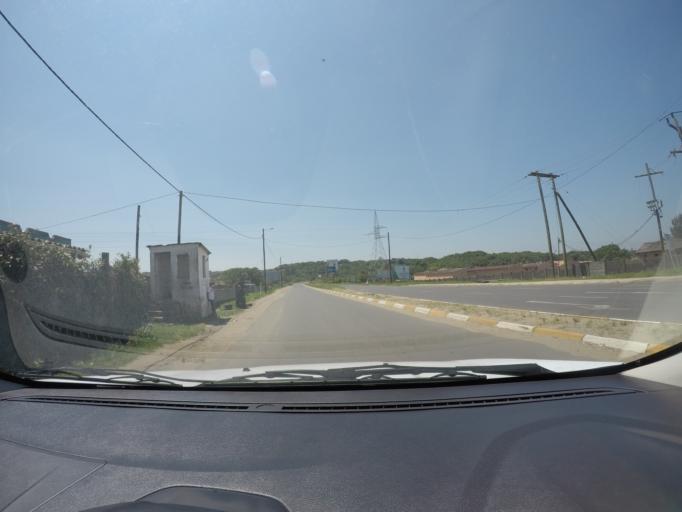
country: ZA
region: KwaZulu-Natal
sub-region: uThungulu District Municipality
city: eSikhawini
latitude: -28.8576
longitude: 31.9232
